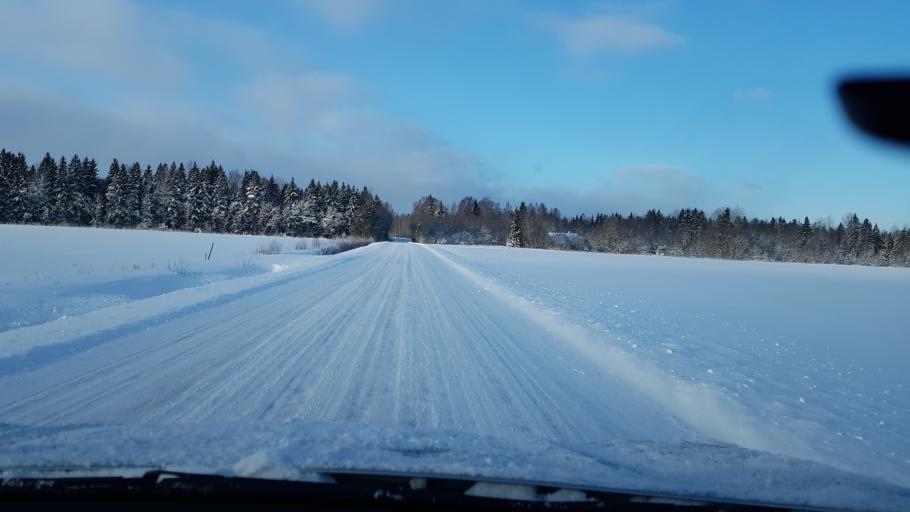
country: EE
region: Harju
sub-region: Nissi vald
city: Turba
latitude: 59.1023
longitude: 24.2469
